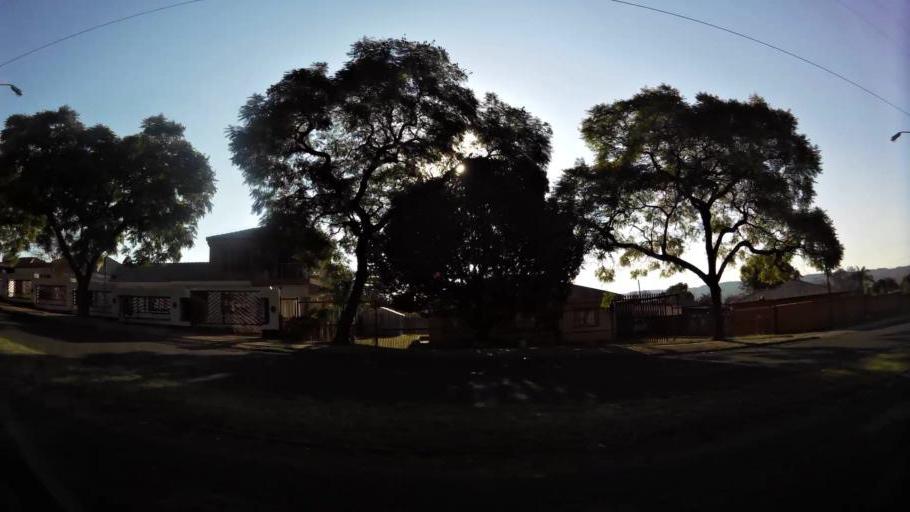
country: ZA
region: Gauteng
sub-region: City of Tshwane Metropolitan Municipality
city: Pretoria
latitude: -25.7541
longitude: 28.1292
